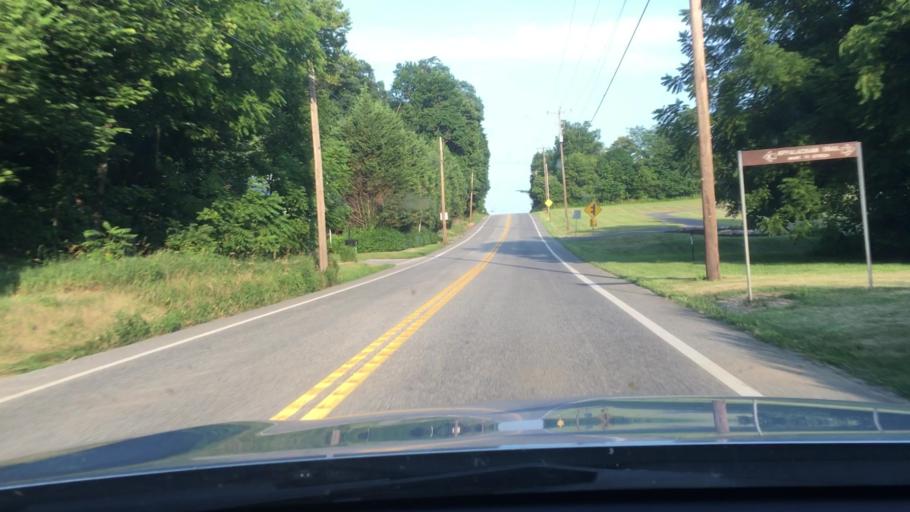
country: US
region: Pennsylvania
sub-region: Cumberland County
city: Boiling Springs
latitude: 40.1729
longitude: -77.1211
